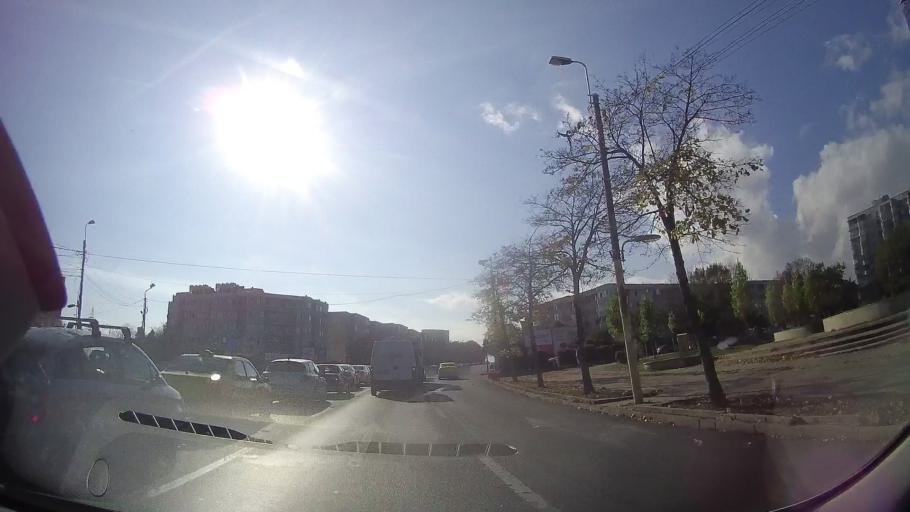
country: RO
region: Constanta
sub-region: Municipiul Constanta
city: Constanta
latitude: 44.1582
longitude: 28.6315
